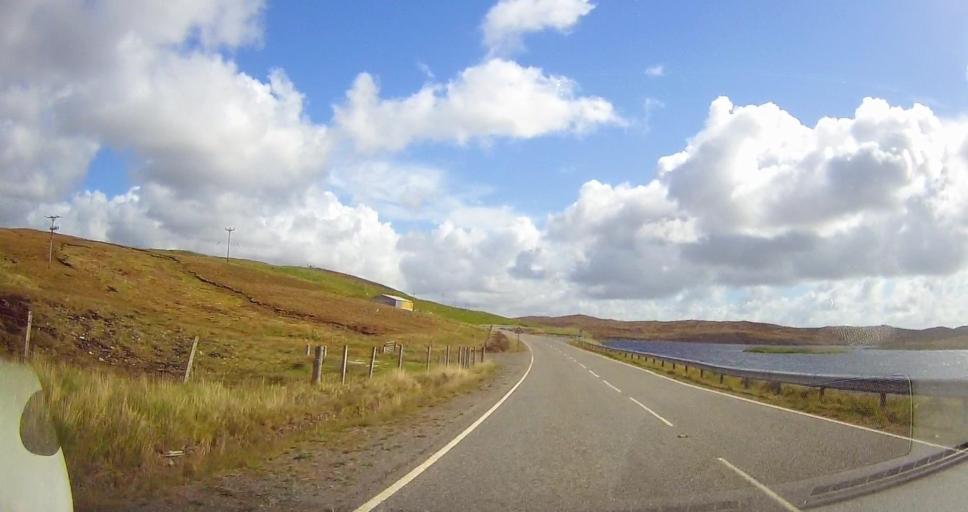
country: GB
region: Scotland
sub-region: Shetland Islands
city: Lerwick
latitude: 60.4677
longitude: -1.4068
